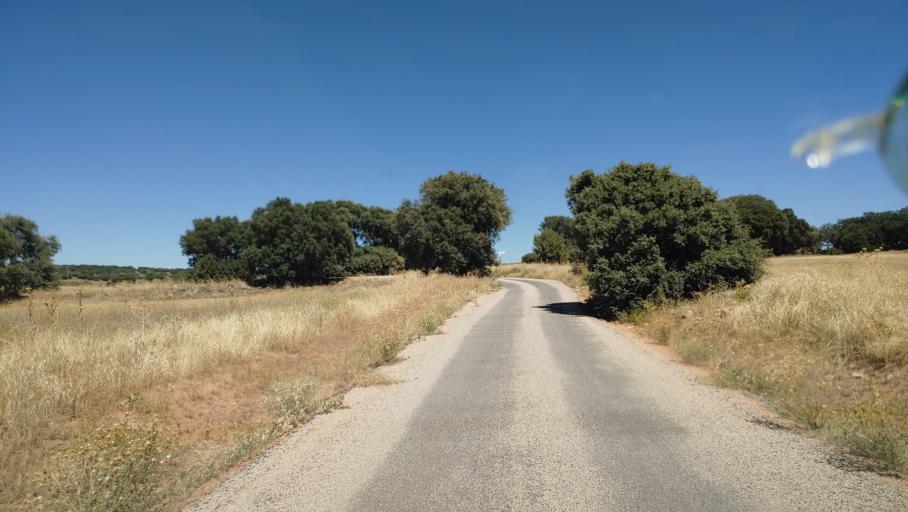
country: ES
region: Castille-La Mancha
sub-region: Provincia de Albacete
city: Ossa de Montiel
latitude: 38.9270
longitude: -2.7856
